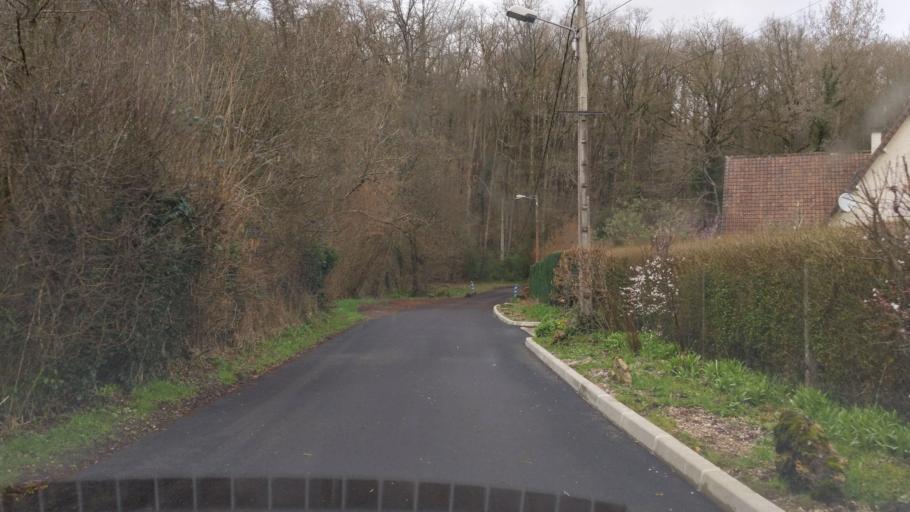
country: FR
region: Ile-de-France
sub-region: Departement de l'Essonne
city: Les Molieres
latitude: 48.6834
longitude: 2.0627
